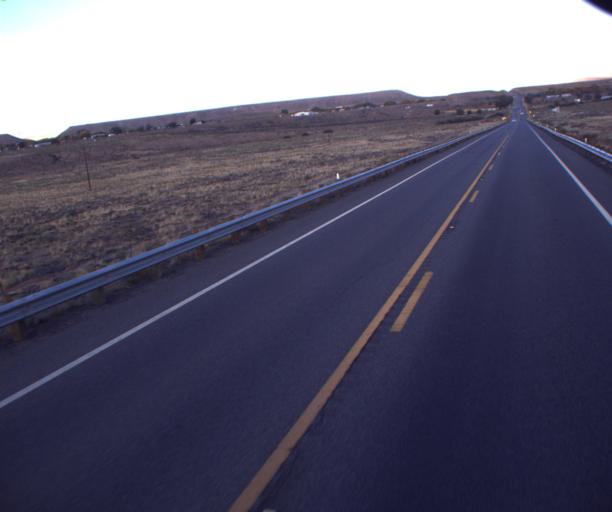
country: US
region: New Mexico
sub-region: San Juan County
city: Shiprock
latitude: 36.9261
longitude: -109.0966
